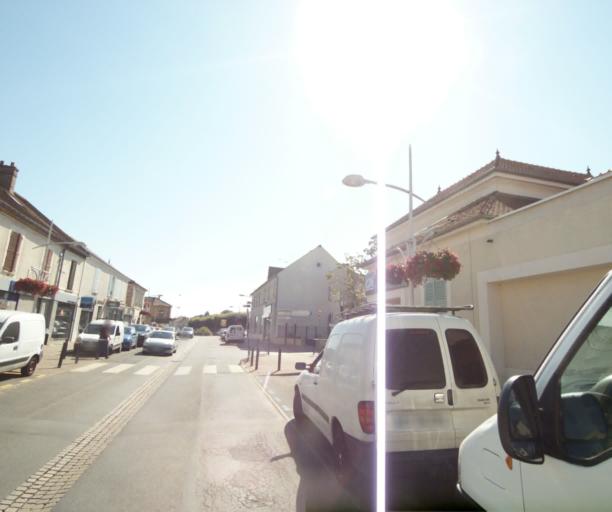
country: FR
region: Ile-de-France
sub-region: Departement de Seine-et-Marne
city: Moissy-Cramayel
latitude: 48.6274
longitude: 2.5919
